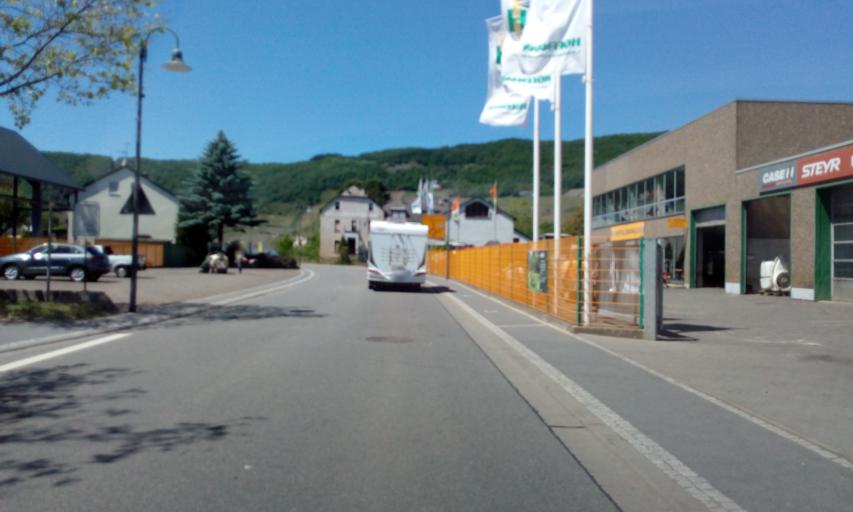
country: DE
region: Rheinland-Pfalz
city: Piesport
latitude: 49.8809
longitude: 6.9226
